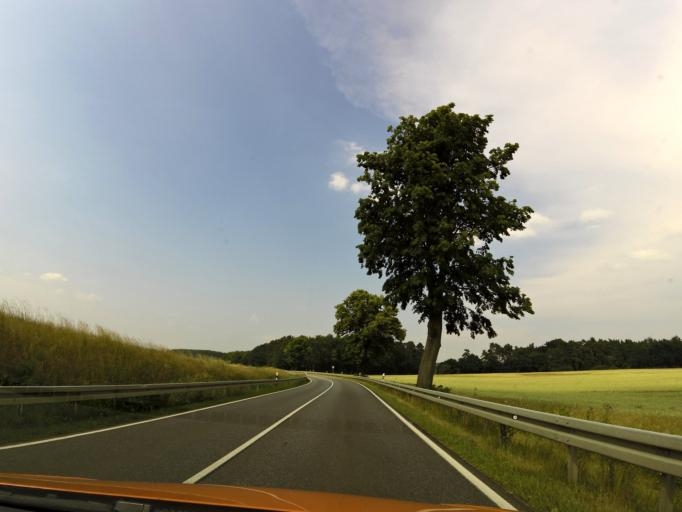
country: DE
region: Mecklenburg-Vorpommern
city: Krakow am See
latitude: 53.7038
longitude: 12.2782
